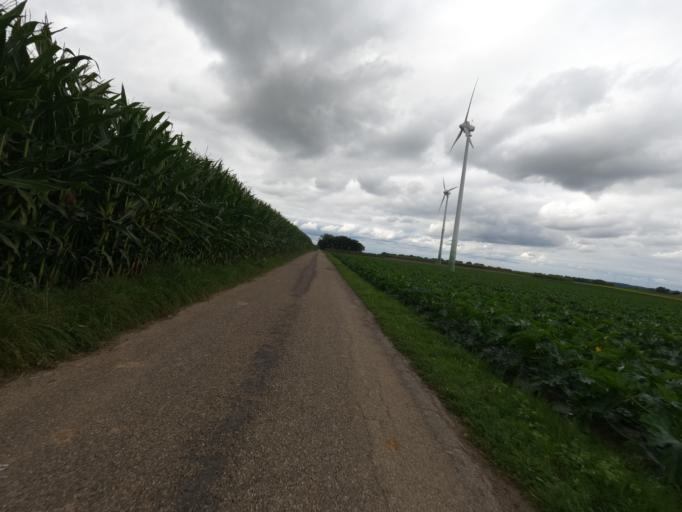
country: DE
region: North Rhine-Westphalia
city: Huckelhoven
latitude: 51.0067
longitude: 6.2178
